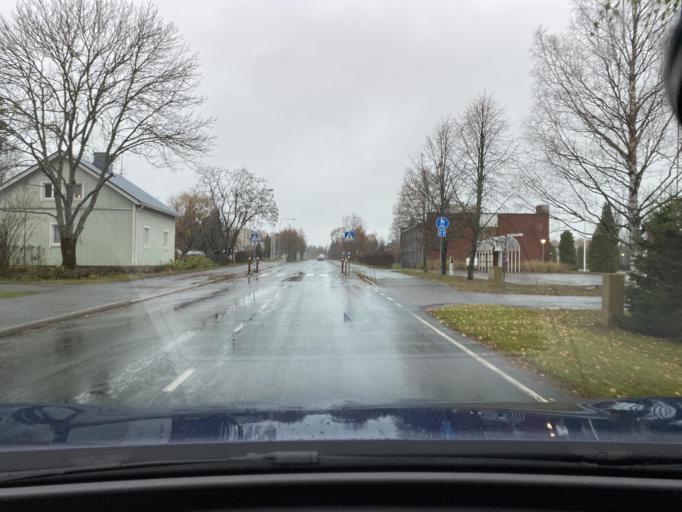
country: FI
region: Varsinais-Suomi
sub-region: Loimaa
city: Alastaro
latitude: 60.9497
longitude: 22.8652
